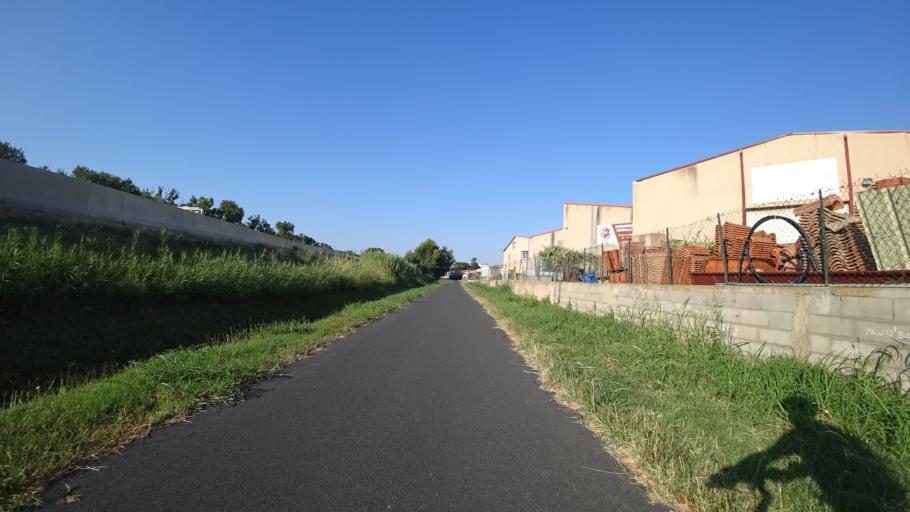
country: FR
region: Languedoc-Roussillon
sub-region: Departement des Pyrenees-Orientales
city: Canet-en-Roussillon
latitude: 42.7073
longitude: 3.0193
